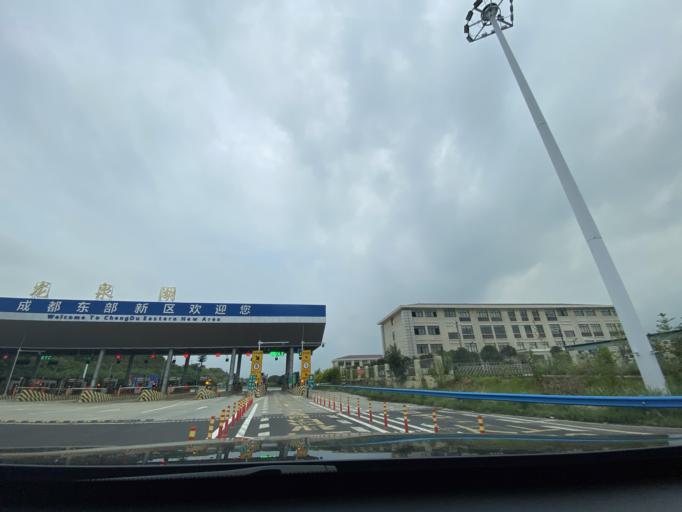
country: CN
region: Sichuan
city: Jiancheng
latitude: 30.4997
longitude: 104.4470
